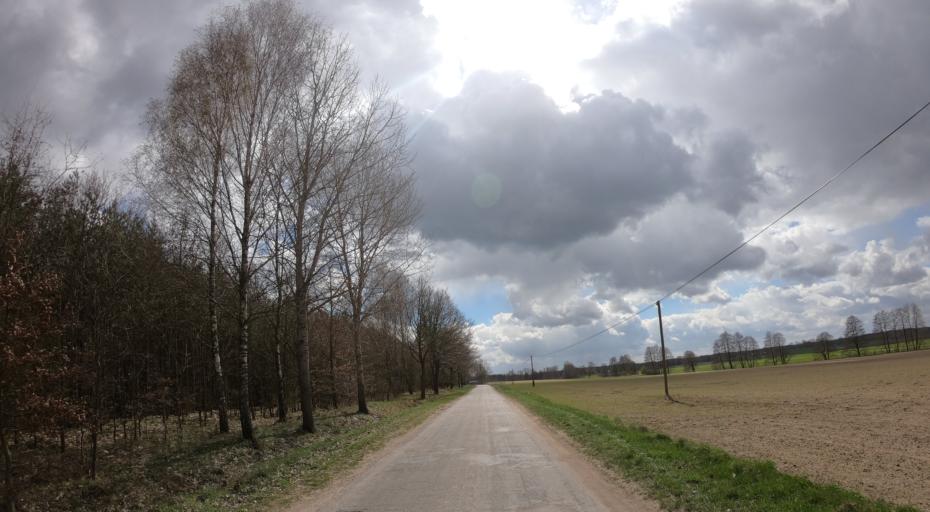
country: PL
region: West Pomeranian Voivodeship
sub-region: Powiat drawski
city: Drawsko Pomorskie
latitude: 53.5331
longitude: 15.8863
